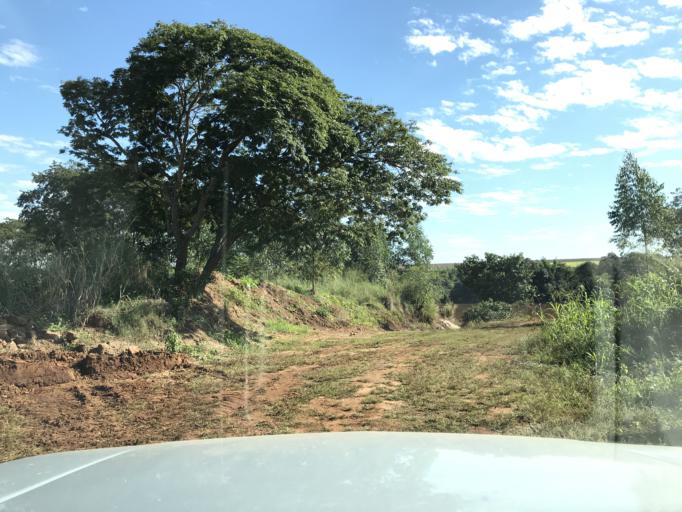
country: BR
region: Parana
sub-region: Ipora
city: Ipora
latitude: -24.1513
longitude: -53.7467
